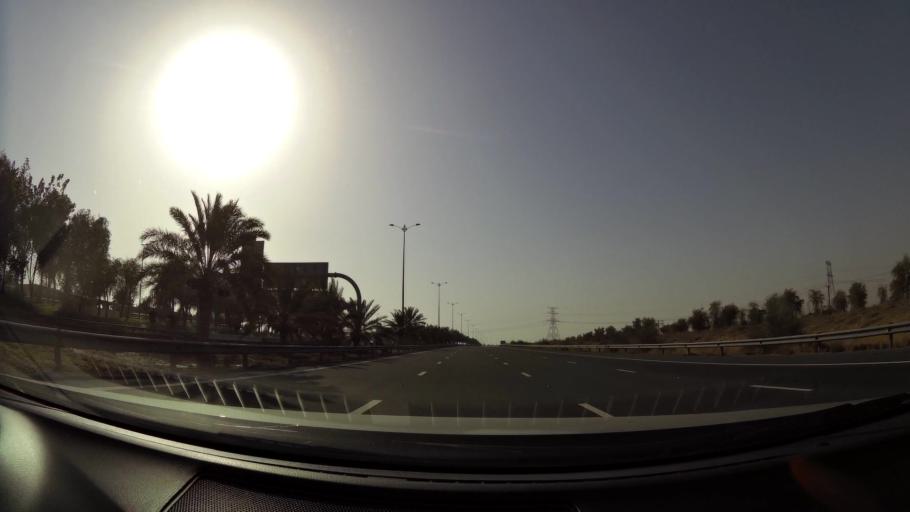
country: OM
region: Al Buraimi
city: Al Buraymi
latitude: 24.6577
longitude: 55.6909
